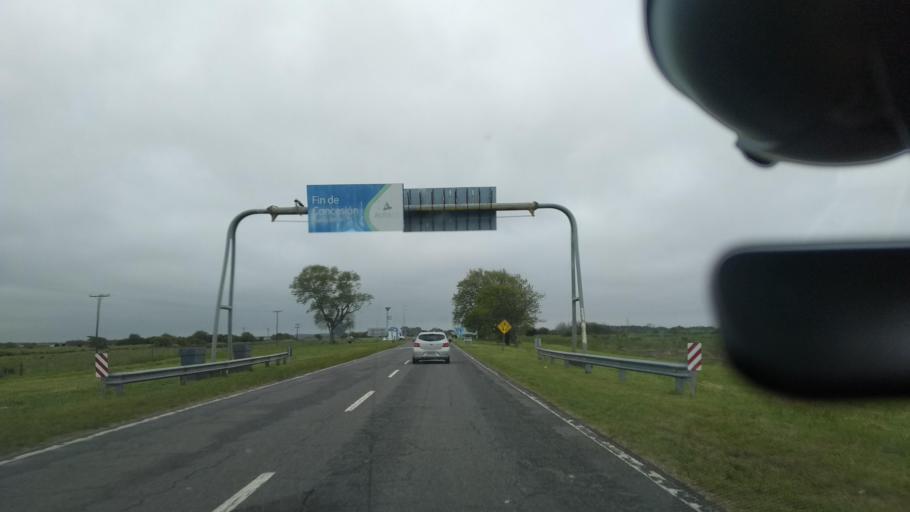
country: AR
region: Buenos Aires
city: Veronica
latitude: -35.5956
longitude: -57.2704
